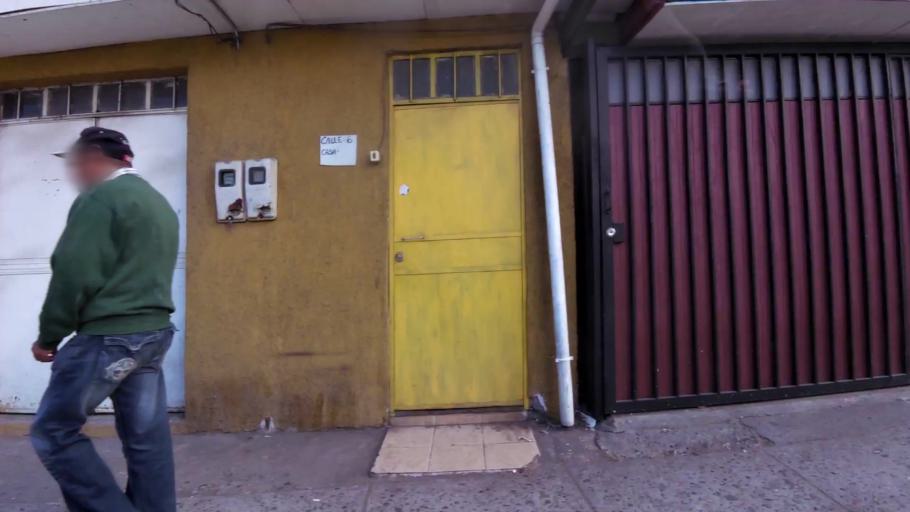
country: CL
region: Biobio
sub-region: Provincia de Concepcion
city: Concepcion
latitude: -36.8045
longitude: -73.0423
